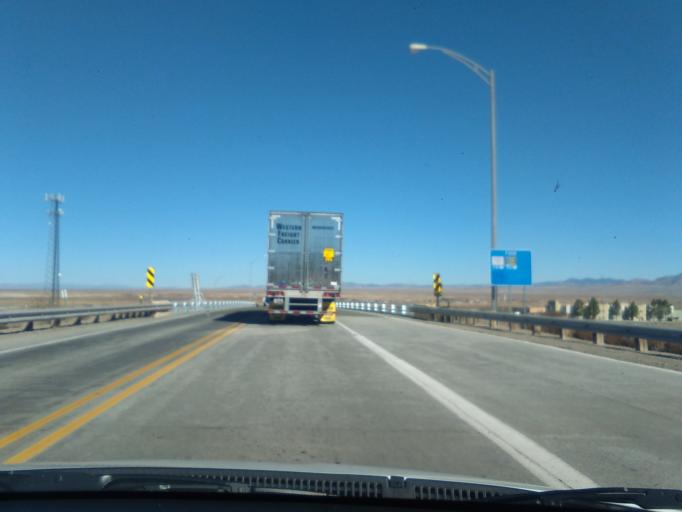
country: US
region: New Mexico
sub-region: Hidalgo County
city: Lordsburg
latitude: 32.3521
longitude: -108.7409
